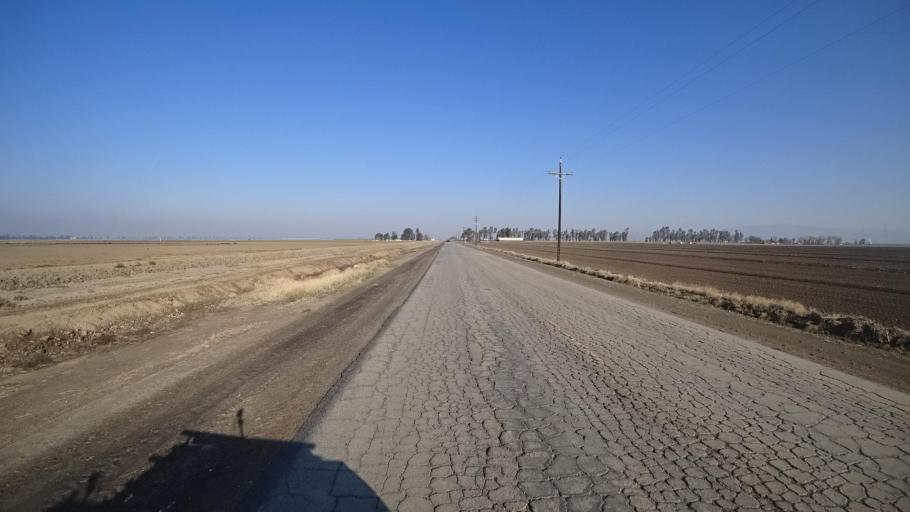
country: US
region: California
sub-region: Kern County
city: Weedpatch
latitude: 35.1802
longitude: -118.9678
